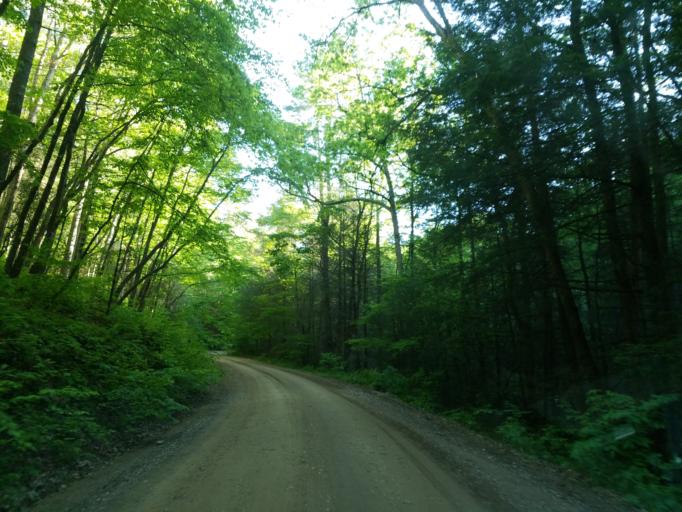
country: US
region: Georgia
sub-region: Lumpkin County
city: Dahlonega
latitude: 34.6973
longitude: -84.1416
